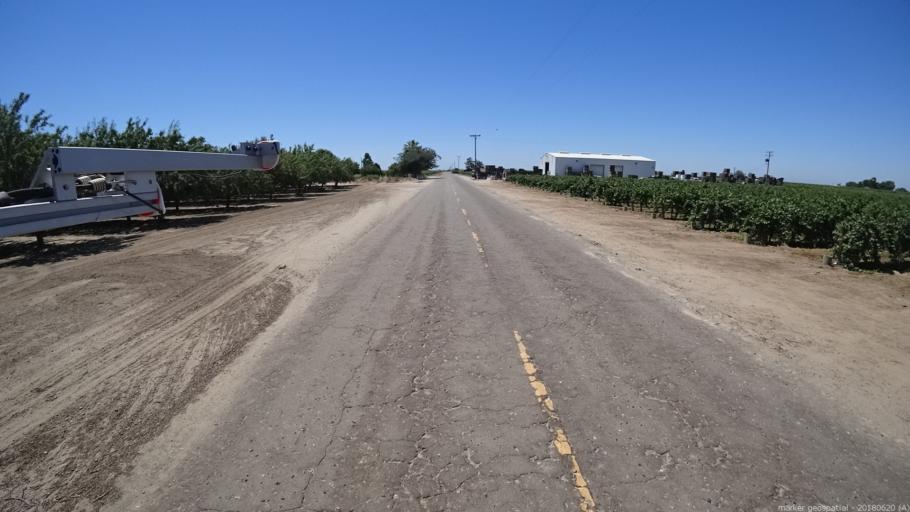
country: US
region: California
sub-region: Fresno County
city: Biola
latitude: 36.8592
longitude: -119.9740
